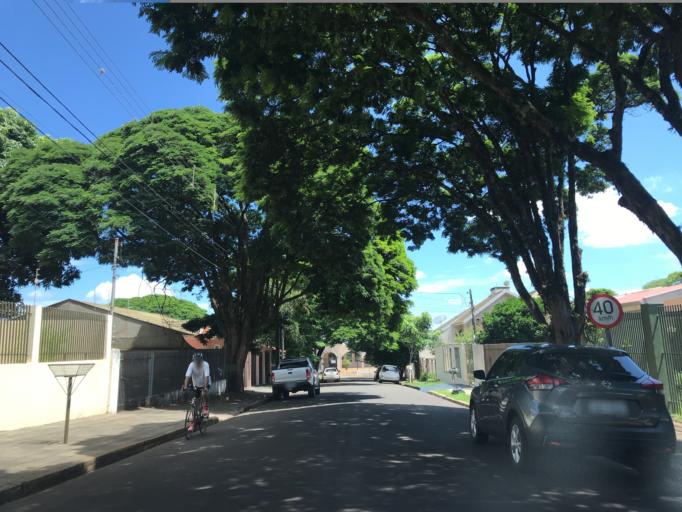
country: BR
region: Parana
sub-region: Maringa
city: Maringa
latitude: -23.4422
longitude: -51.9565
